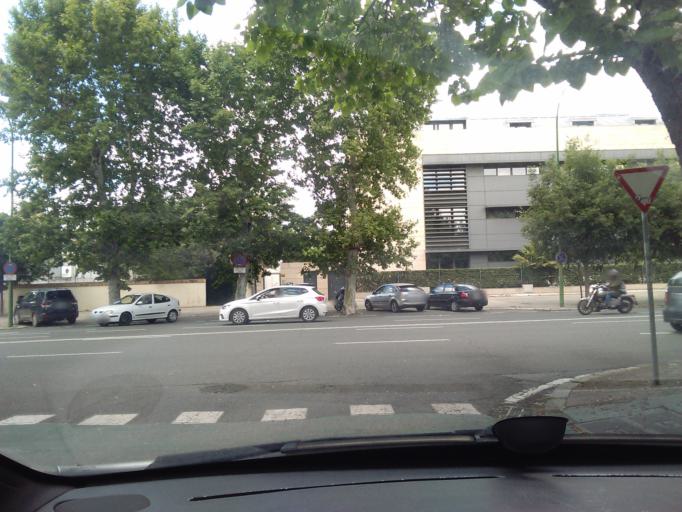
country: ES
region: Andalusia
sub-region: Provincia de Sevilla
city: Sevilla
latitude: 37.3633
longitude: -5.9854
